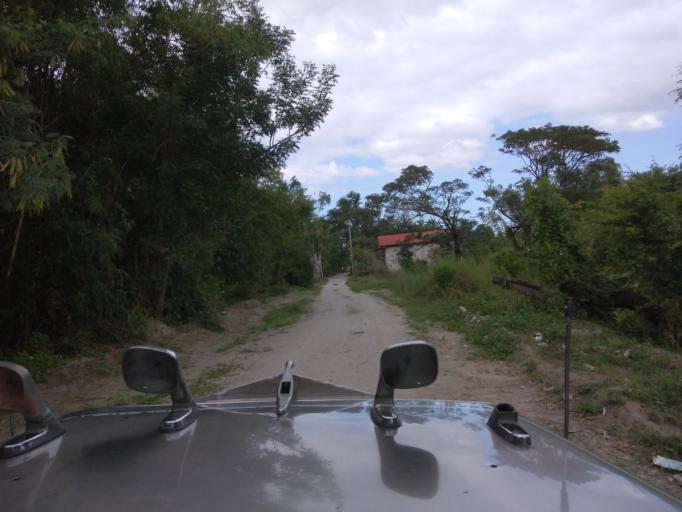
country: PH
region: Central Luzon
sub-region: Province of Pampanga
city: San Patricio
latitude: 15.1149
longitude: 120.7109
